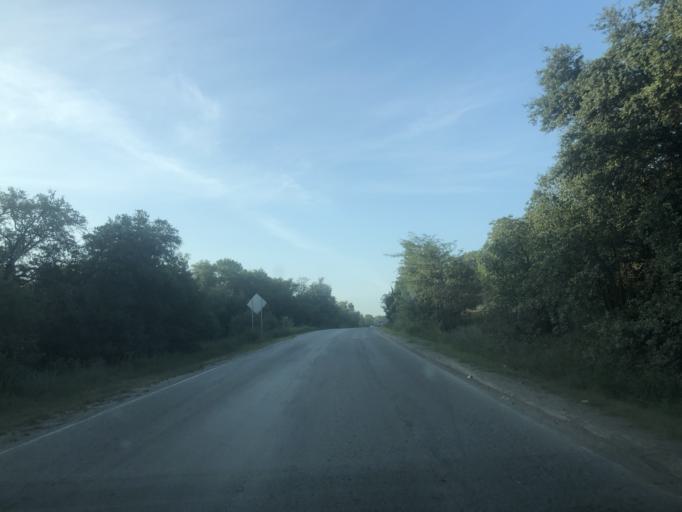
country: US
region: Texas
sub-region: Tarrant County
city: Lakeside
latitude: 32.7906
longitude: -97.4912
